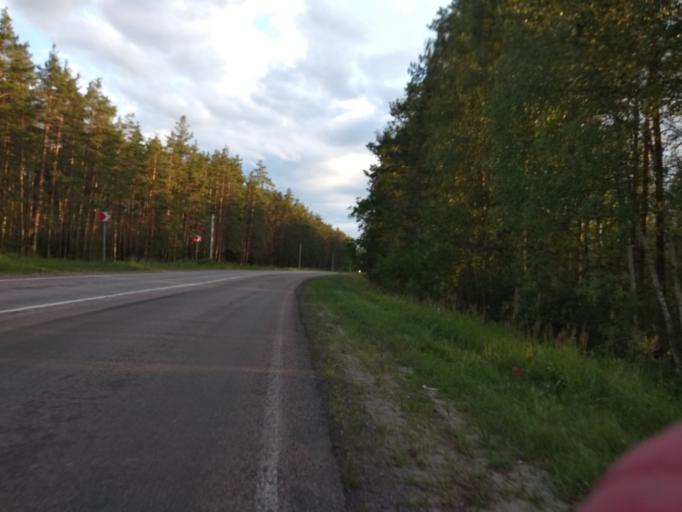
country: RU
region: Moskovskaya
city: Misheronskiy
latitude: 55.6271
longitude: 39.7390
